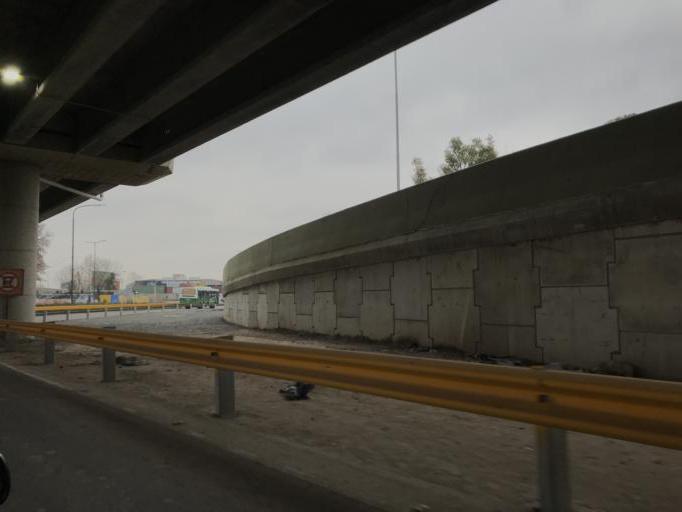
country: AR
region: Buenos Aires F.D.
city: Retiro
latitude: -34.5773
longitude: -58.3879
